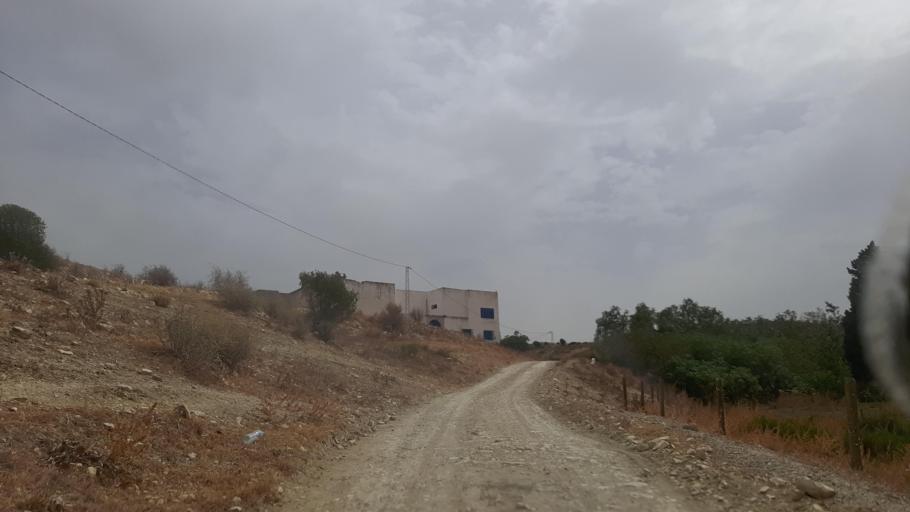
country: TN
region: Tunis
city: La Mohammedia
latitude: 36.5693
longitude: 10.1384
